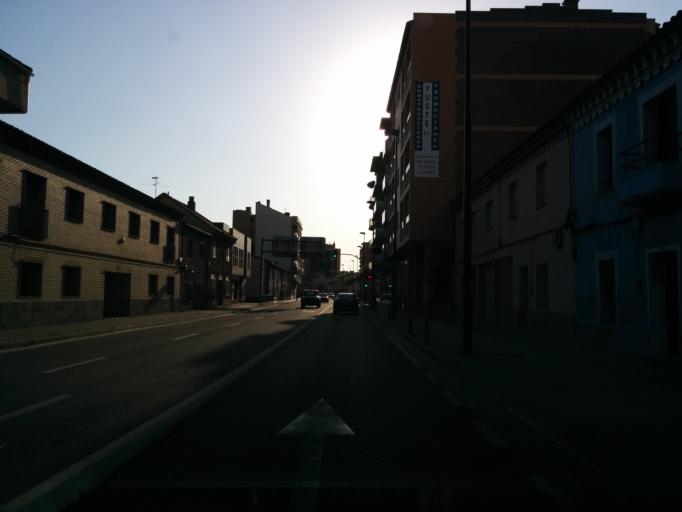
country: ES
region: Aragon
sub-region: Provincia de Zaragoza
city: Zaragoza
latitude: 41.6667
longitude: -0.8260
